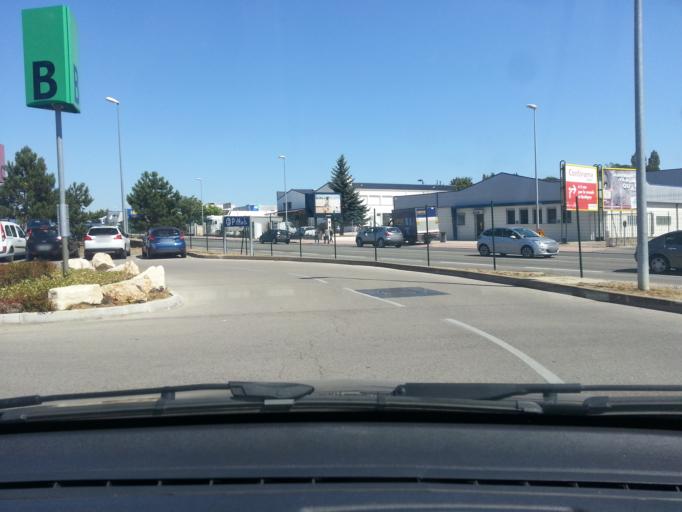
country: FR
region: Bourgogne
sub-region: Departement de la Cote-d'Or
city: Saint-Apollinaire
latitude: 47.3392
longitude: 5.0641
